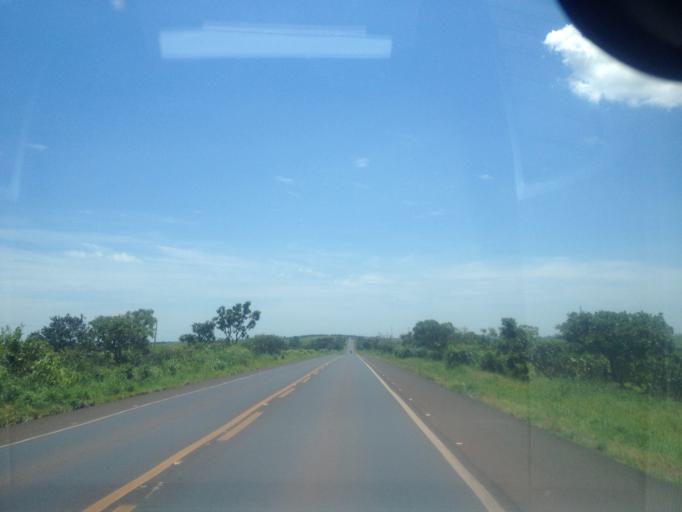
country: BR
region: Minas Gerais
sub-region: Ituiutaba
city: Ituiutaba
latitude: -18.8911
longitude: -49.2336
